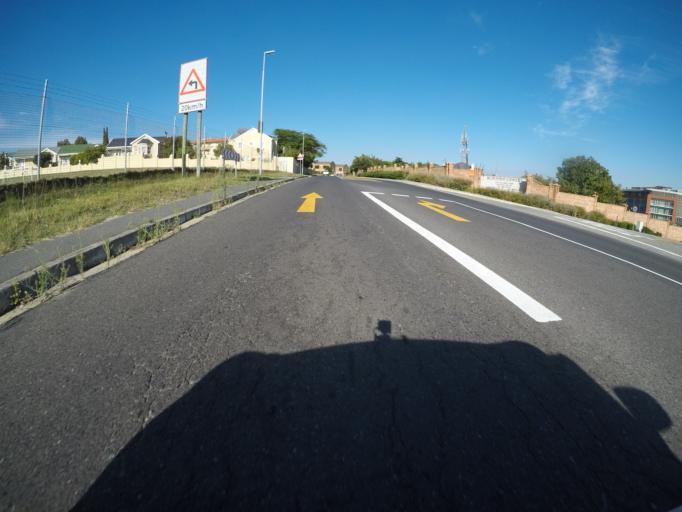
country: ZA
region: Western Cape
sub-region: City of Cape Town
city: Kraaifontein
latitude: -33.8809
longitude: 18.6427
